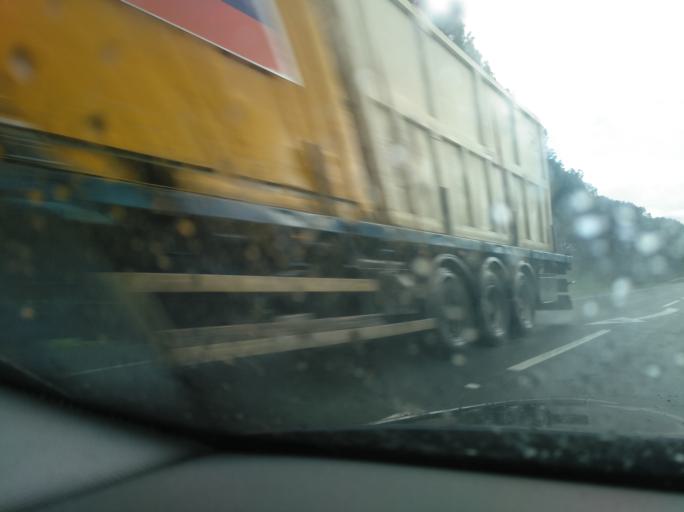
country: PT
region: Setubal
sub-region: Grandola
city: Grandola
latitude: 38.0834
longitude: -8.4174
